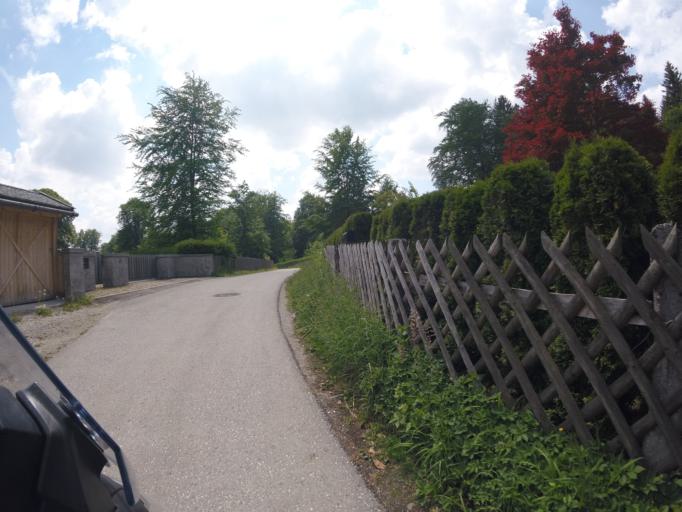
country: DE
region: Bavaria
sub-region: Upper Bavaria
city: Icking
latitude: 47.9367
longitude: 11.4283
